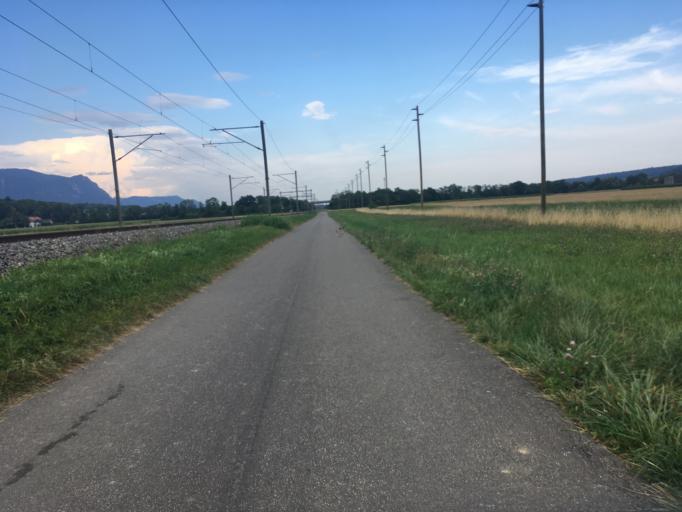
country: CH
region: Solothurn
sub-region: Bezirk Lebern
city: Bettlach
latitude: 47.1960
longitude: 7.4343
